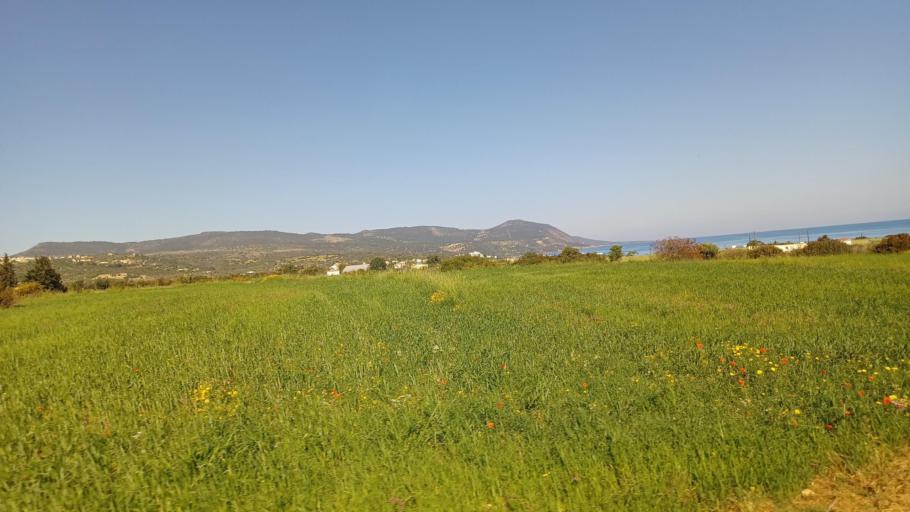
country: CY
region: Pafos
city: Polis
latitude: 35.0362
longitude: 32.3940
